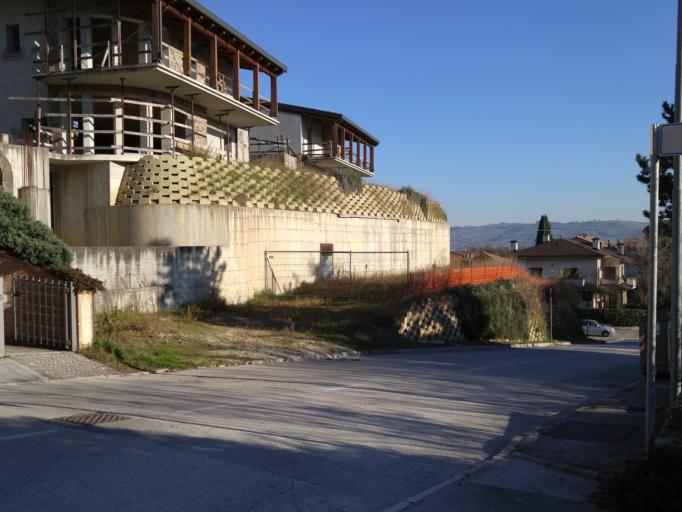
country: IT
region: The Marches
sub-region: Provincia di Pesaro e Urbino
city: Calcinelli
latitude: 43.7540
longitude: 12.9191
